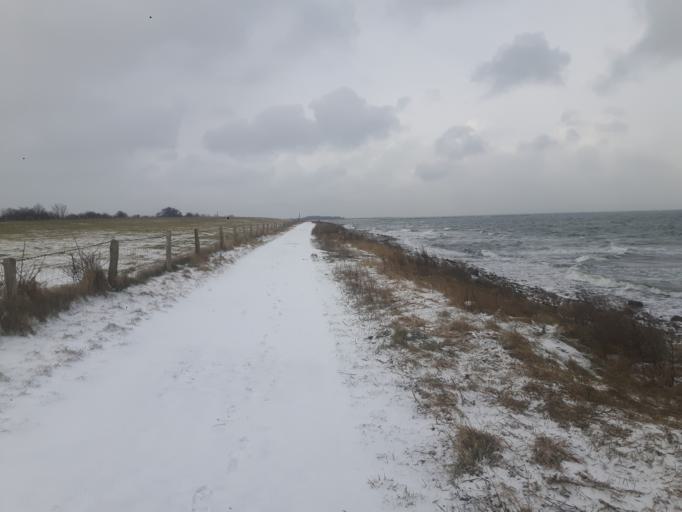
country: DE
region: Schleswig-Holstein
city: Fehmarn
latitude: 54.5047
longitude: 11.2154
